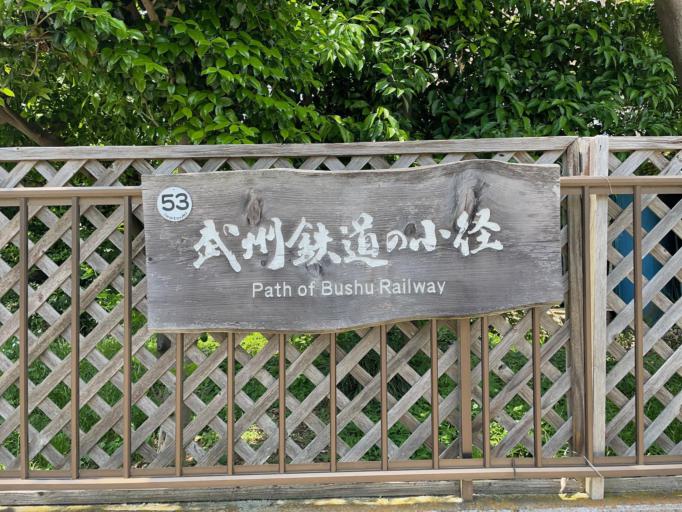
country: JP
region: Saitama
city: Iwatsuki
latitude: 35.9543
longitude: 139.7001
